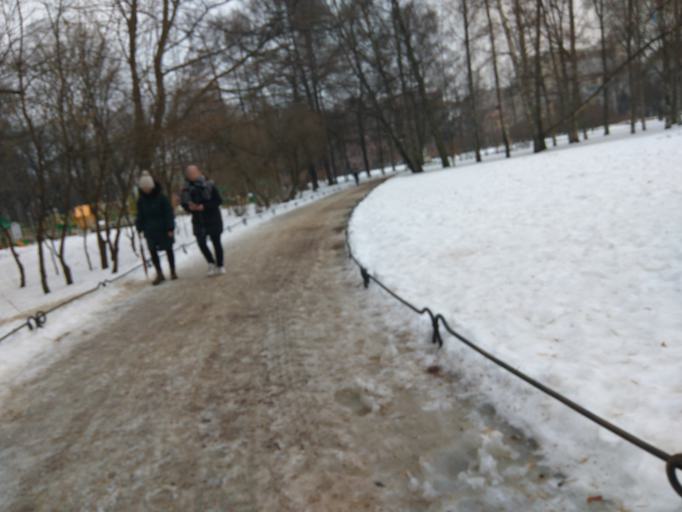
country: RU
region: St.-Petersburg
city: Centralniy
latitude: 59.9445
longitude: 30.3713
